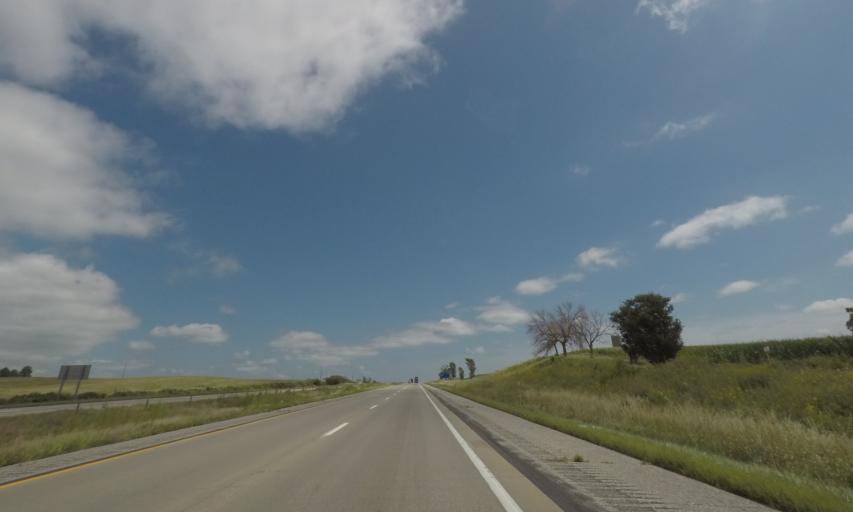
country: US
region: Iowa
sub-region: Iowa County
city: Williamsburg
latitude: 41.6871
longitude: -92.0401
